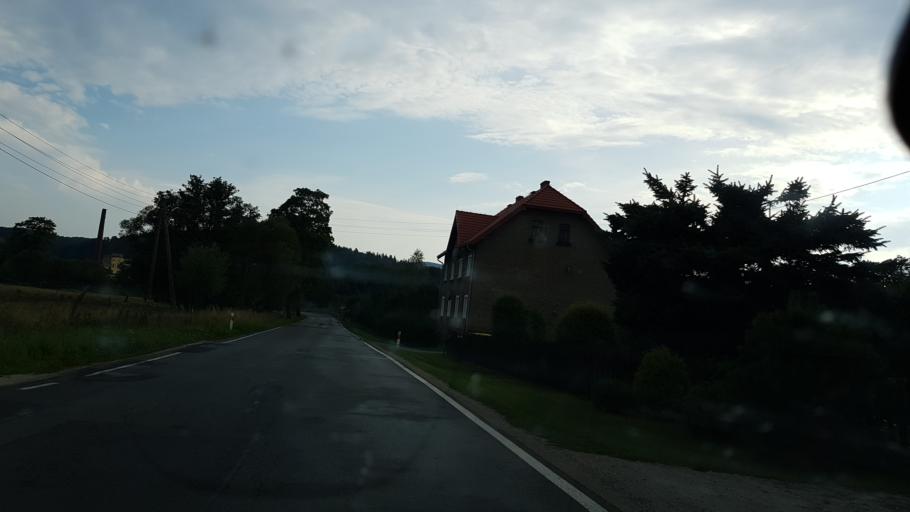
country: PL
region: Lower Silesian Voivodeship
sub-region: Powiat kamiennogorski
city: Marciszow
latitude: 50.8573
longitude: 16.0023
